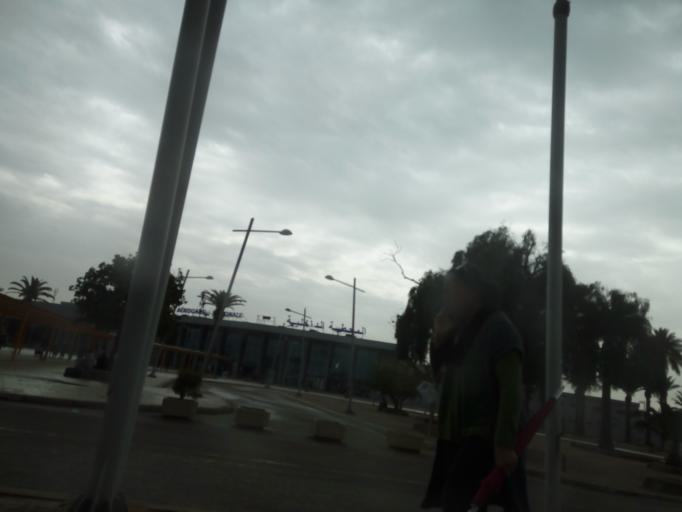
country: DZ
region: Alger
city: Dar el Beida
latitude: 36.7011
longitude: 3.2109
